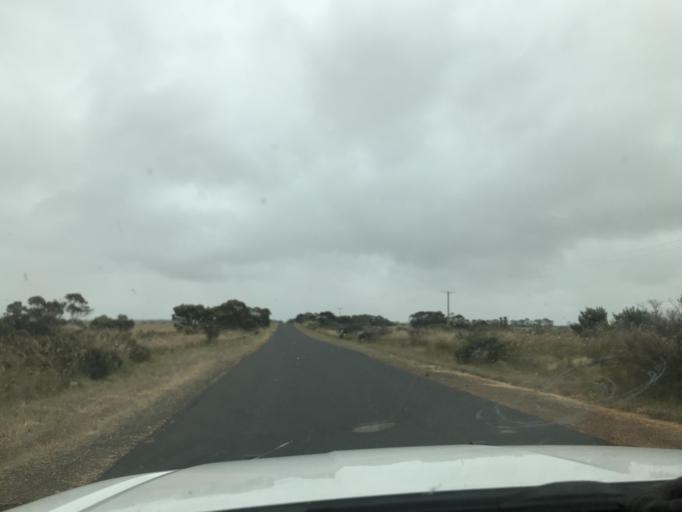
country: AU
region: South Australia
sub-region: Tatiara
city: Bordertown
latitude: -36.1169
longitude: 141.0356
